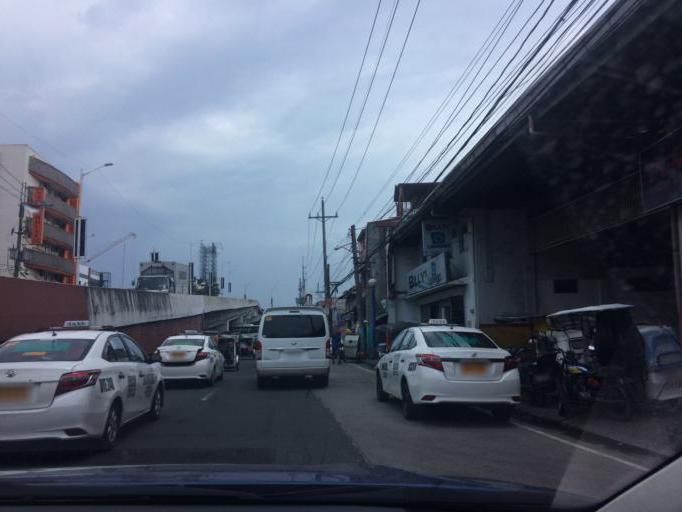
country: PH
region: Metro Manila
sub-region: Makati City
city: Makati City
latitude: 14.5356
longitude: 121.0034
